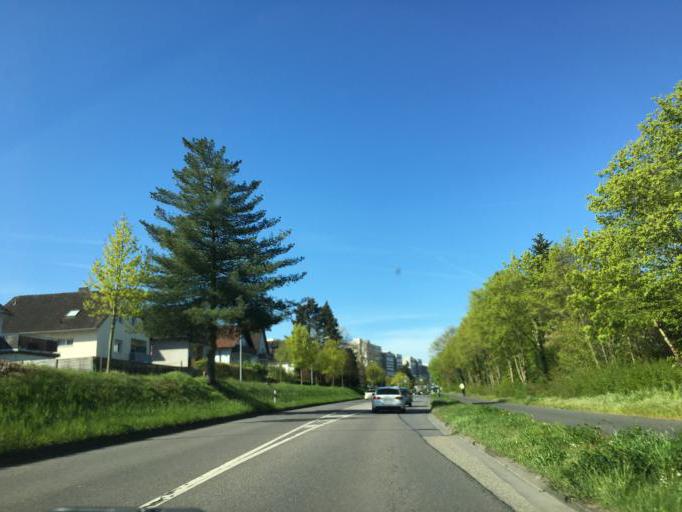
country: DE
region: Hesse
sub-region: Regierungsbezirk Darmstadt
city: Rodgau
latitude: 50.0042
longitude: 8.8703
